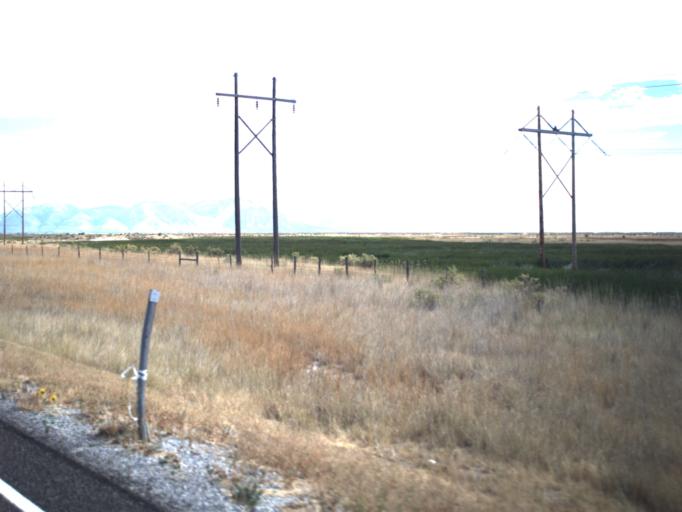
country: US
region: Utah
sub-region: Box Elder County
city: Tremonton
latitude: 41.6110
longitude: -112.3511
